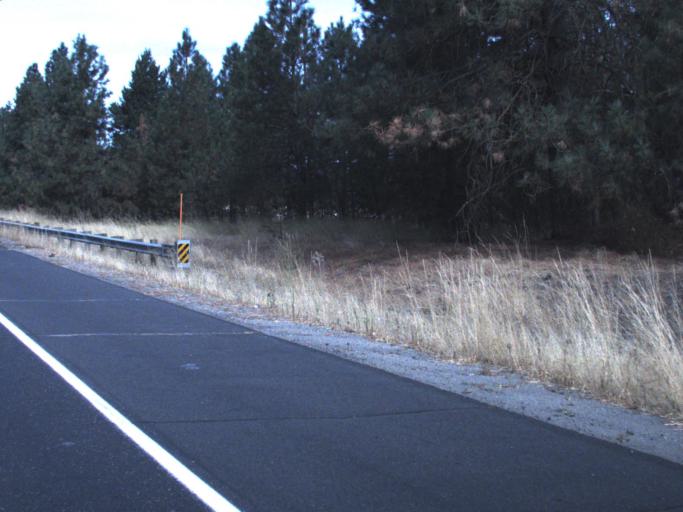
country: US
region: Washington
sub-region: Spokane County
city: Deer Park
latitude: 47.9235
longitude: -117.4589
